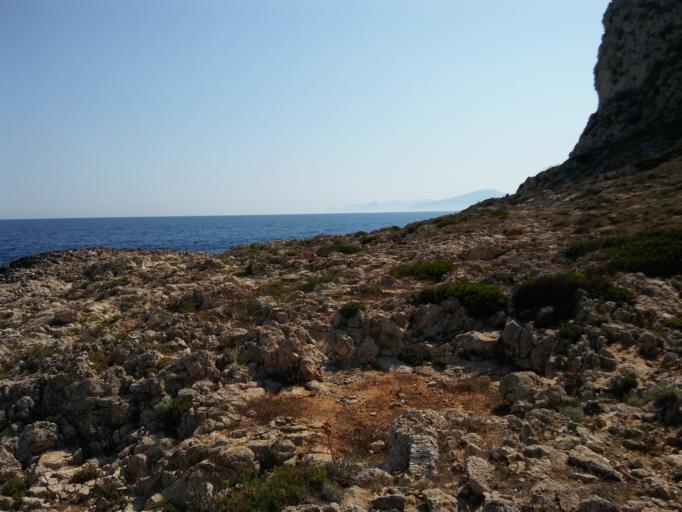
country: IT
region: Sicily
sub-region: Trapani
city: Favignana
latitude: 37.9985
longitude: 12.3462
